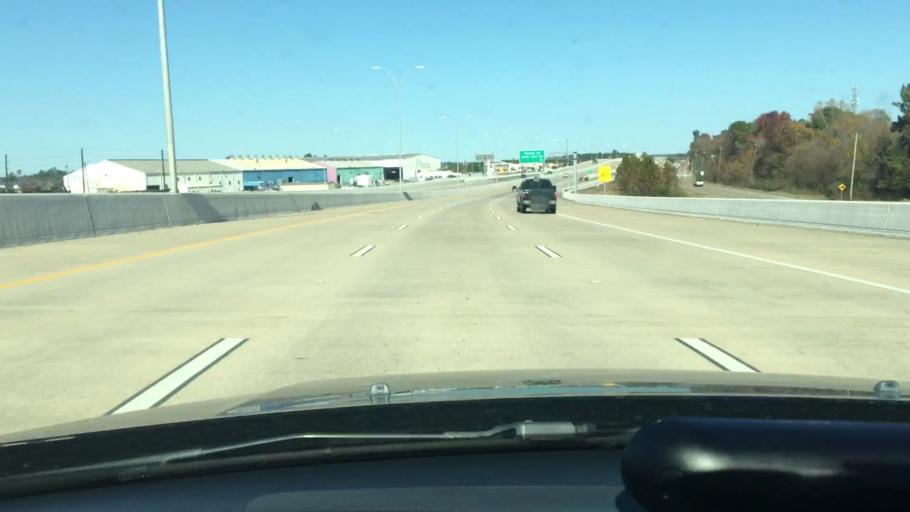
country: US
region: Texas
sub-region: Harris County
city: Sheldon
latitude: 29.8455
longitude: -95.1863
